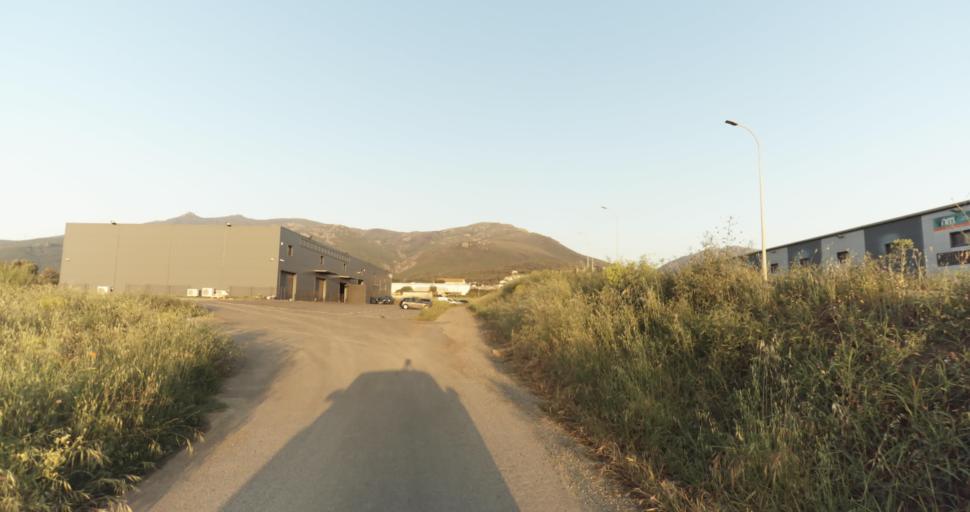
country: FR
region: Corsica
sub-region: Departement de la Haute-Corse
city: Biguglia
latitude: 42.5942
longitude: 9.4419
